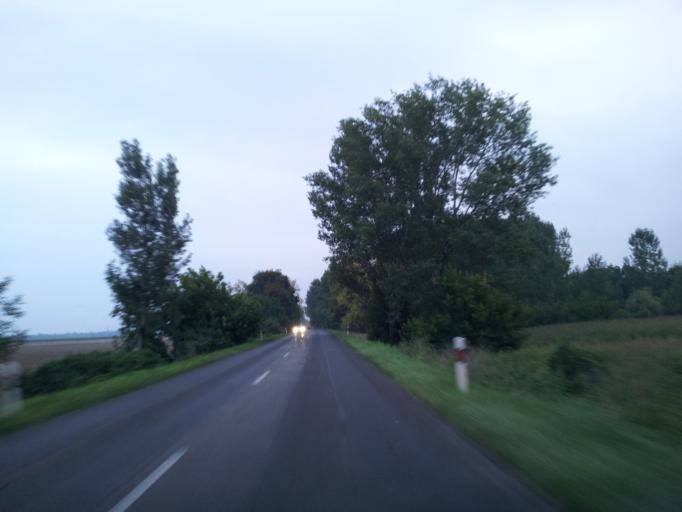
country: HU
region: Tolna
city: Tolna
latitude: 46.4372
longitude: 18.8074
